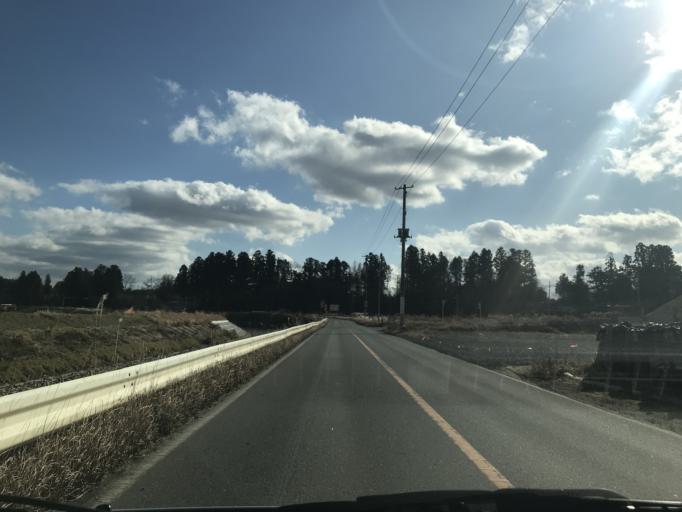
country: JP
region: Miyagi
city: Kogota
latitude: 38.7226
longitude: 141.0648
